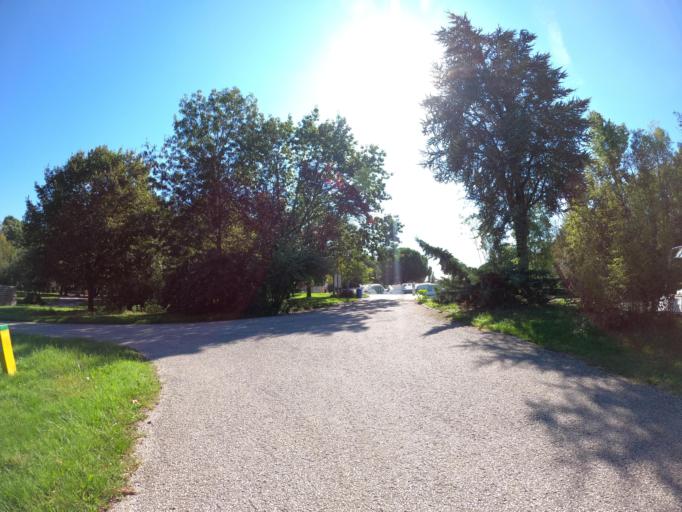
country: FR
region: Aquitaine
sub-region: Departement du Lot-et-Garonne
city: Bon-Encontre
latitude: 44.1774
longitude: 0.6640
